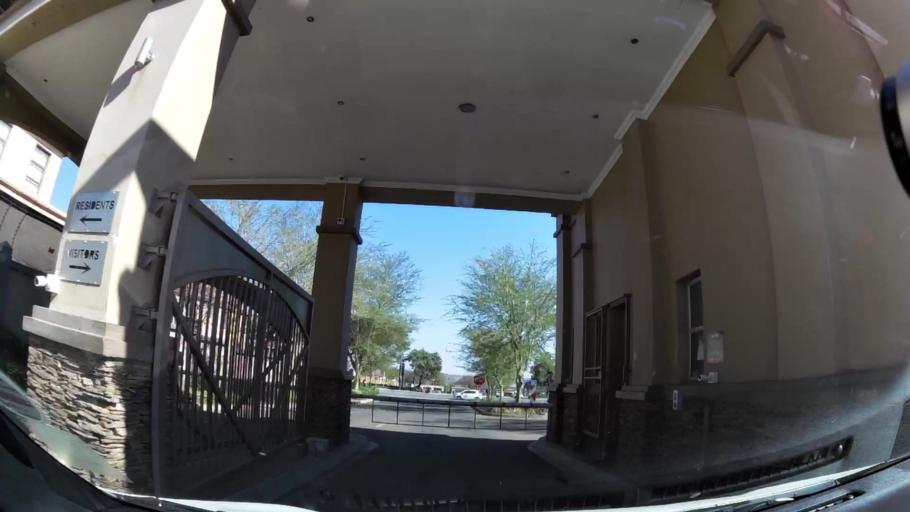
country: ZA
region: Gauteng
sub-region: City of Johannesburg Metropolitan Municipality
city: Midrand
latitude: -25.9353
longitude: 28.1319
